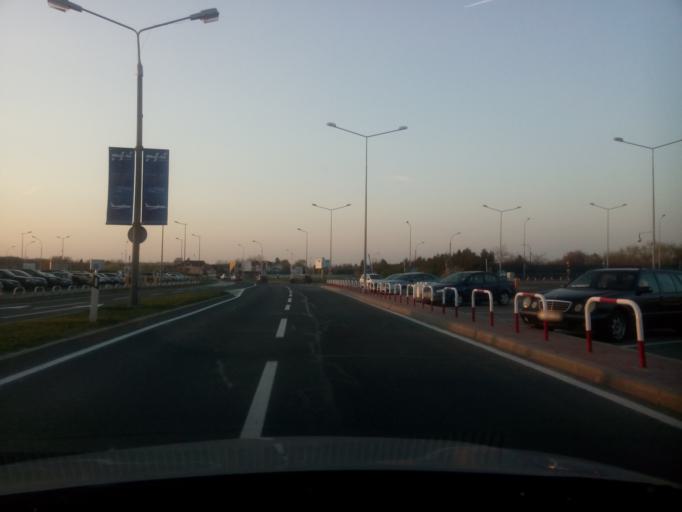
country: RO
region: Ilfov
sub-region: Comuna Otopeni
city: Otopeni
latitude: 44.5714
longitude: 26.0755
